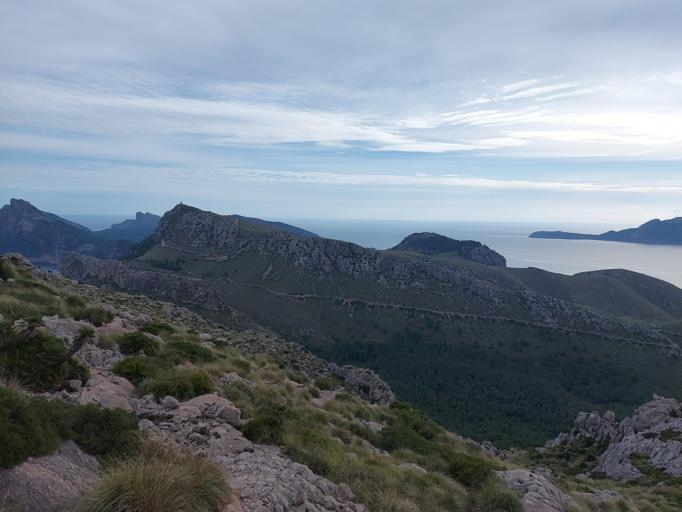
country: ES
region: Balearic Islands
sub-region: Illes Balears
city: Alcudia
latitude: 39.9232
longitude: 3.0945
